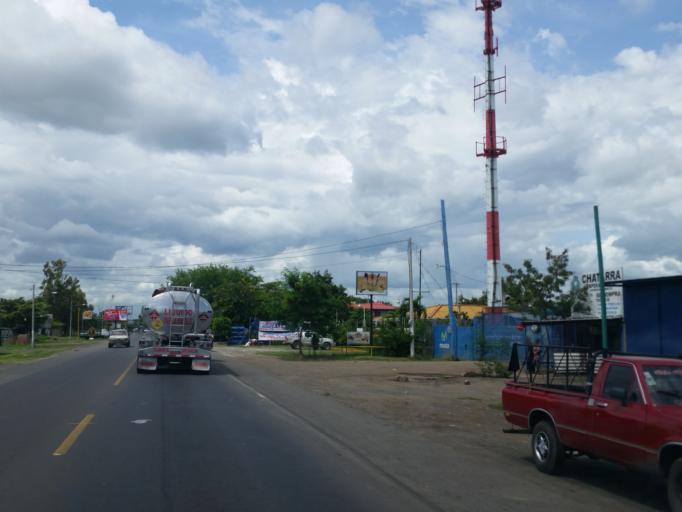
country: NI
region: Managua
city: Tipitapa
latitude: 12.1914
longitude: -86.1055
